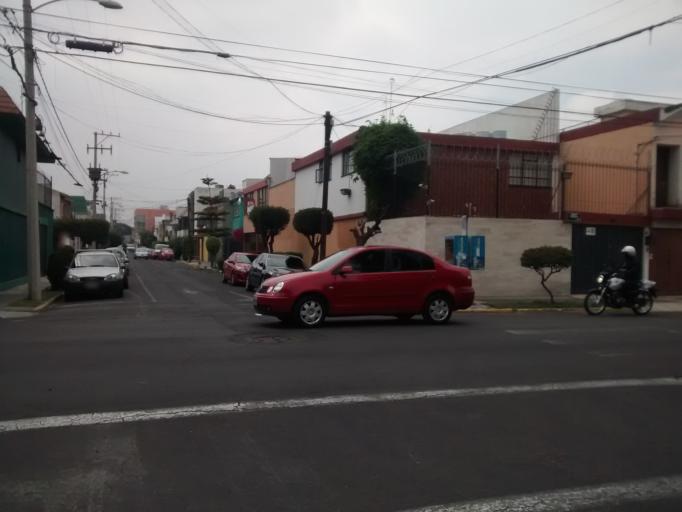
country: MX
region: Mexico
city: Colonia Lindavista
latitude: 19.4935
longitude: -99.1357
